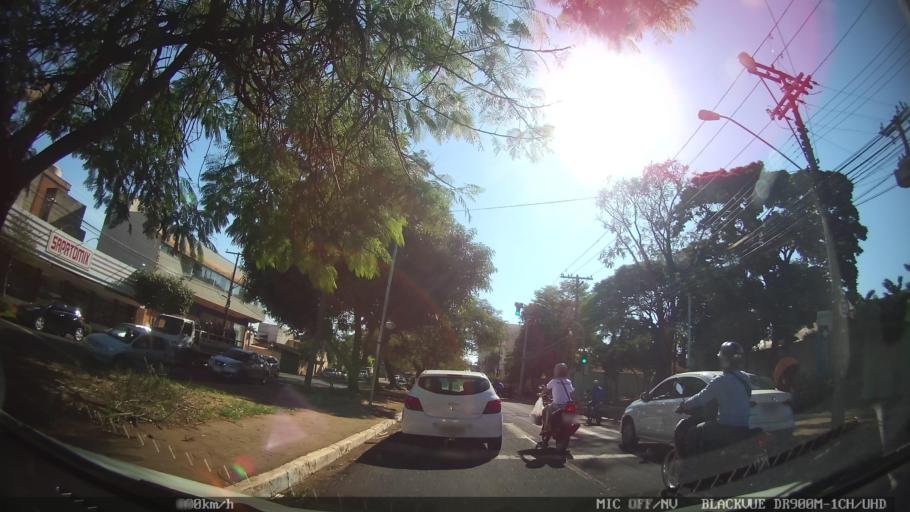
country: BR
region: Sao Paulo
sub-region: Ribeirao Preto
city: Ribeirao Preto
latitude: -21.1765
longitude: -47.7913
